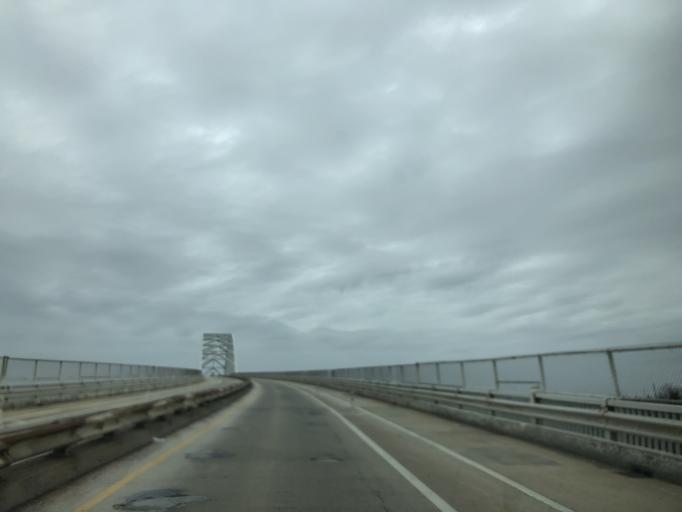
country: US
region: Delaware
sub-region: New Castle County
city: Delaware City
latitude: 39.5498
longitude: -75.6492
